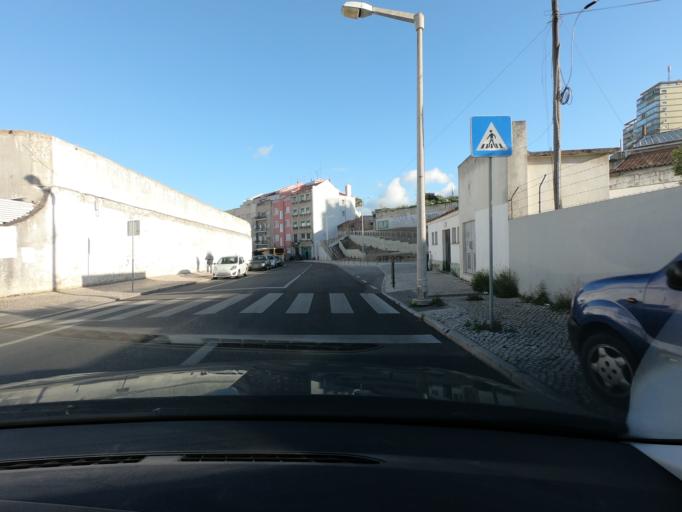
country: PT
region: Lisbon
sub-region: Lisbon
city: Lisbon
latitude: 38.7271
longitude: -9.1146
